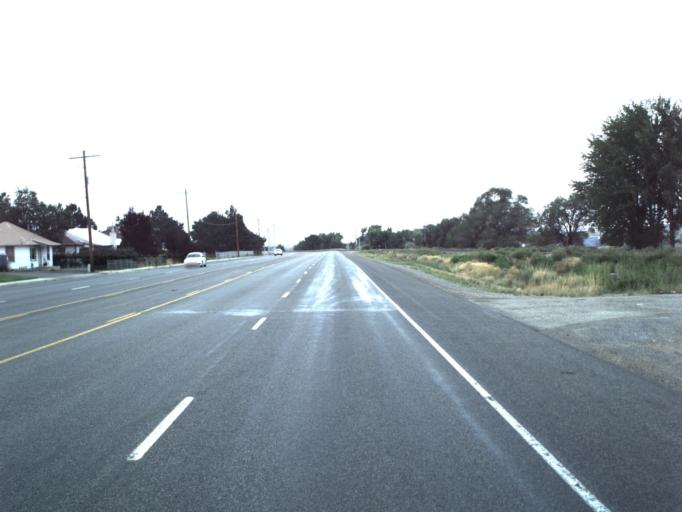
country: US
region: Utah
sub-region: Carbon County
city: Price
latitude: 39.5786
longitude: -110.7860
